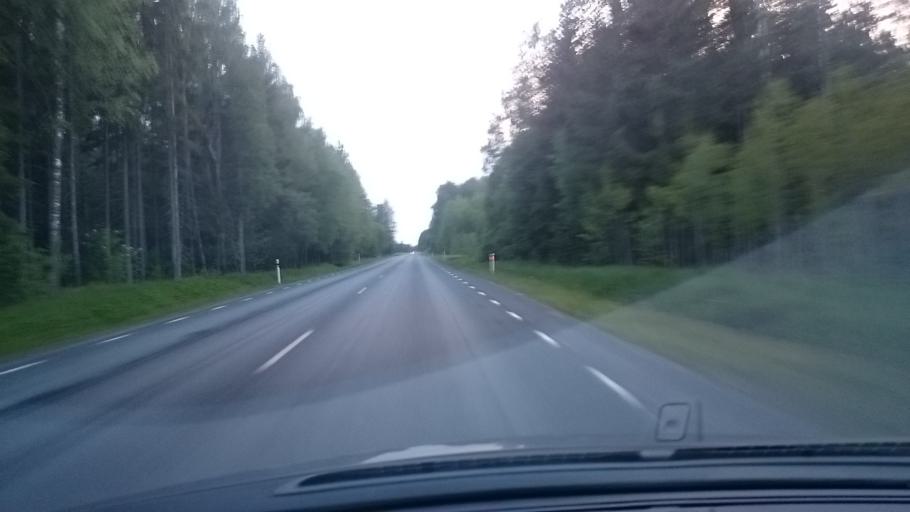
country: EE
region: Paernumaa
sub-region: Vaendra vald (alev)
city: Vandra
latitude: 58.8340
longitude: 25.0907
